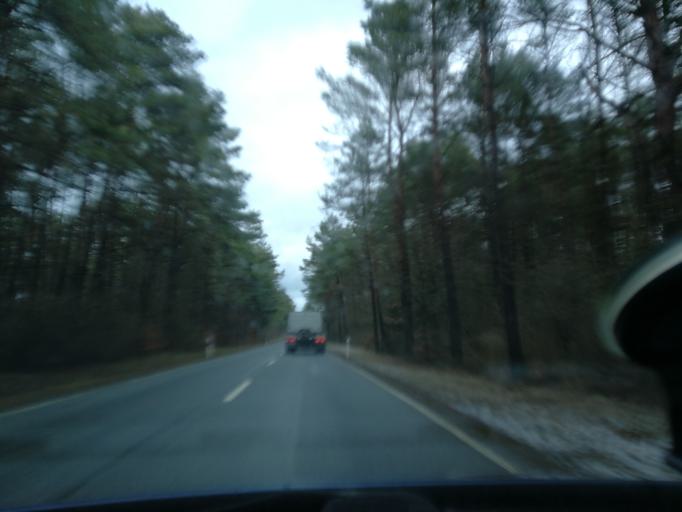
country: DE
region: Rheinland-Pfalz
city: Oberehe-Stroheich
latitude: 50.3004
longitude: 6.7595
